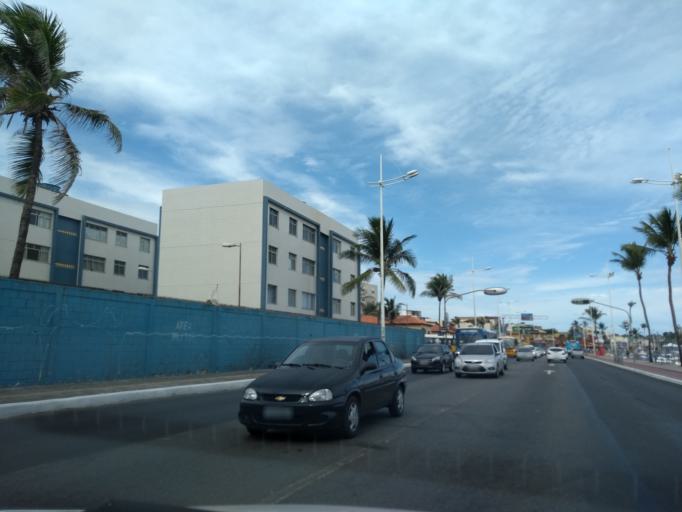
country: BR
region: Bahia
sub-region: Lauro De Freitas
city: Lauro de Freitas
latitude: -12.9510
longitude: -38.3713
